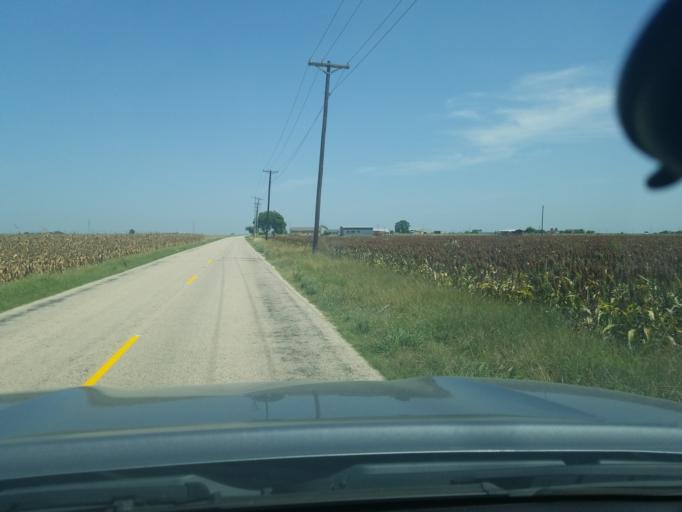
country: US
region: Texas
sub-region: Guadalupe County
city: Lake Dunlap
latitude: 29.6830
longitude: -98.0311
